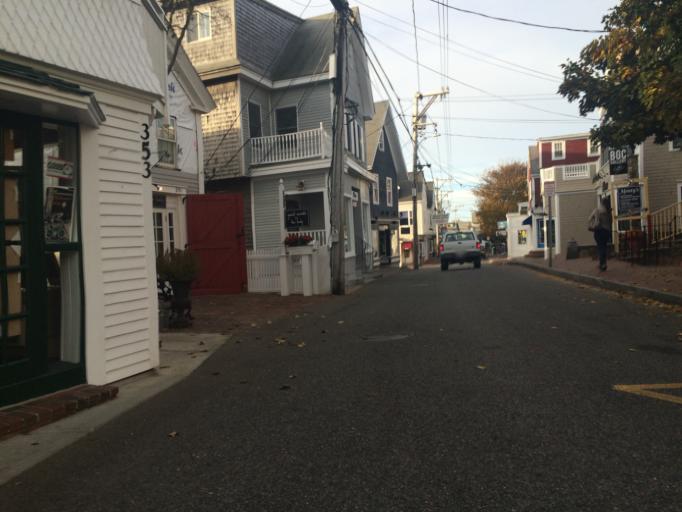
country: US
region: Massachusetts
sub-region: Barnstable County
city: Provincetown
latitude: 42.0532
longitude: -70.1842
